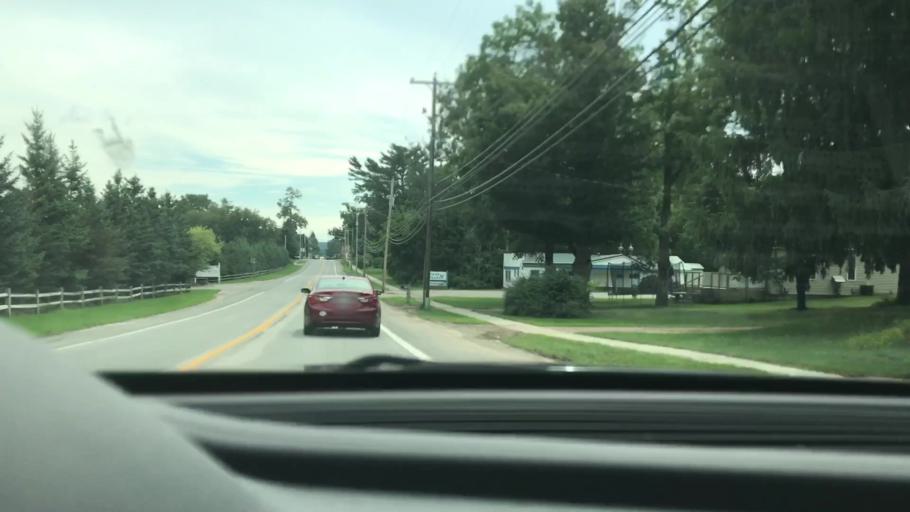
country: US
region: Michigan
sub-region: Antrim County
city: Bellaire
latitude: 45.0757
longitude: -85.2642
